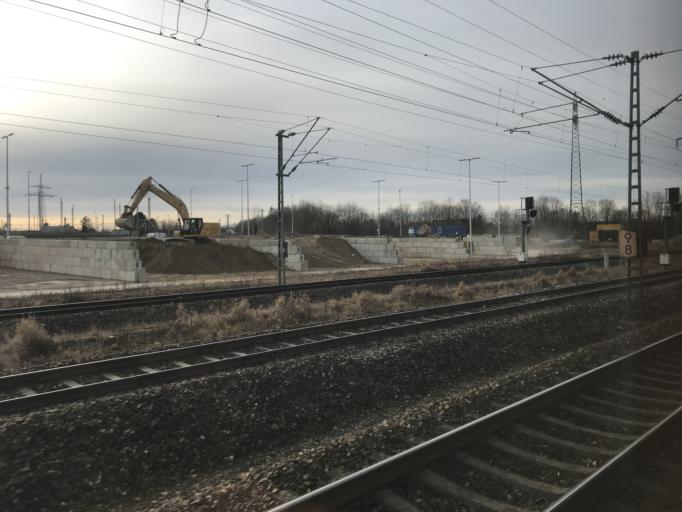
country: DE
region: Bavaria
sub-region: Upper Bavaria
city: Pasing
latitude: 48.1620
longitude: 11.4347
